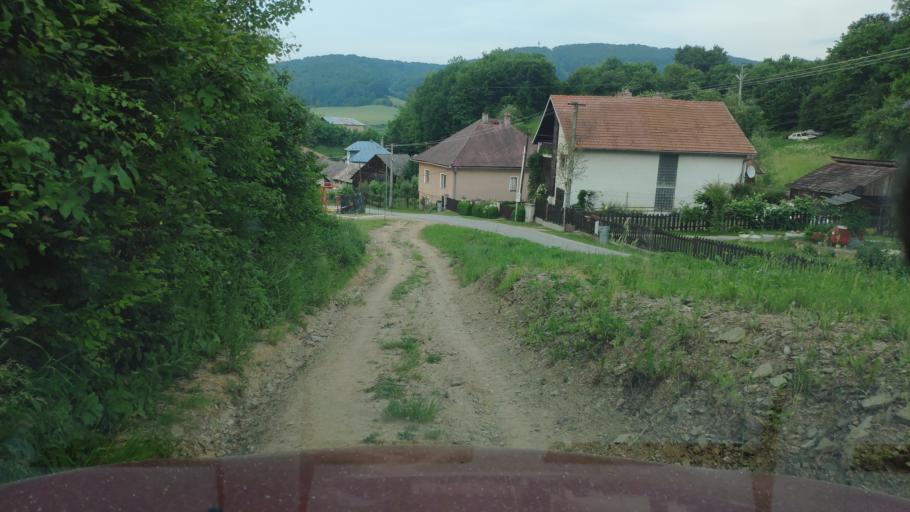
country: SK
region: Presovsky
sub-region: Okres Presov
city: Presov
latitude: 48.9584
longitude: 21.1398
